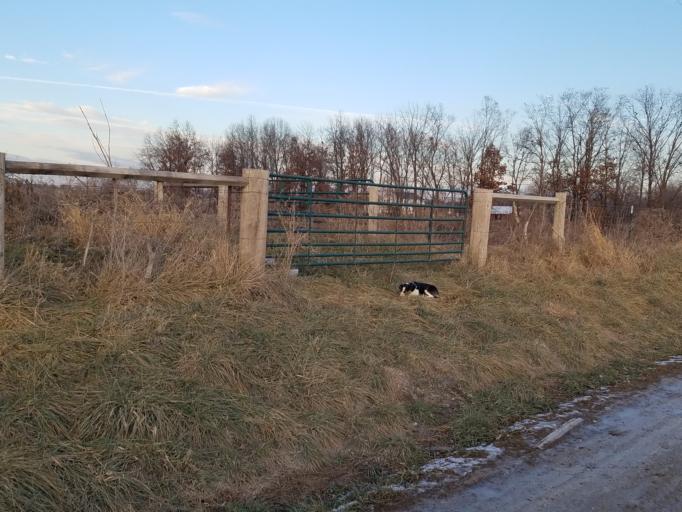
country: US
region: Missouri
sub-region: Randolph County
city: Moberly
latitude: 39.3181
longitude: -92.2906
